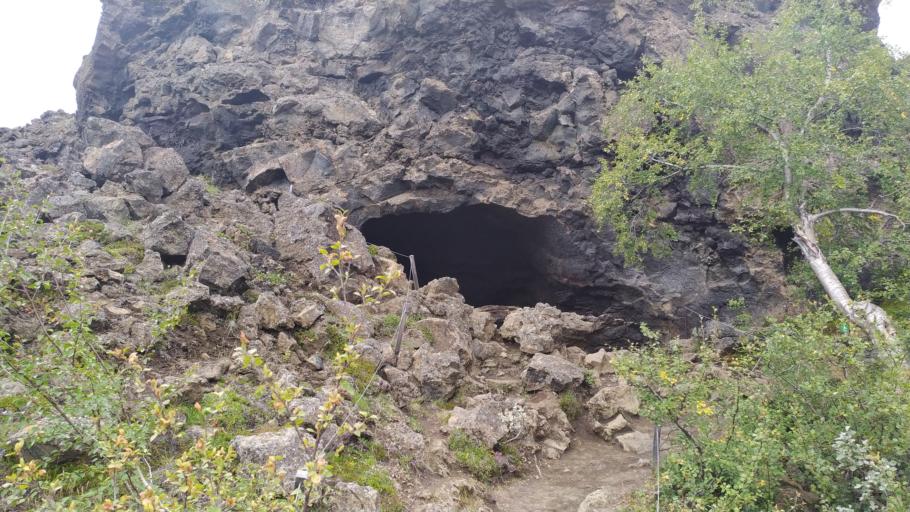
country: IS
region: Northeast
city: Laugar
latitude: 65.5901
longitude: -16.9102
